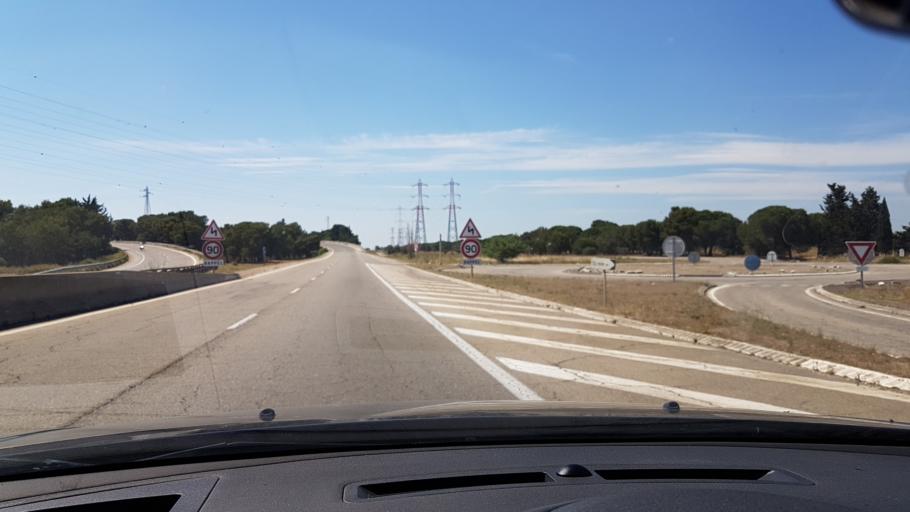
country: FR
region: Provence-Alpes-Cote d'Azur
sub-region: Departement des Bouches-du-Rhone
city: Fos-sur-Mer
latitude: 43.4767
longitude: 4.8992
